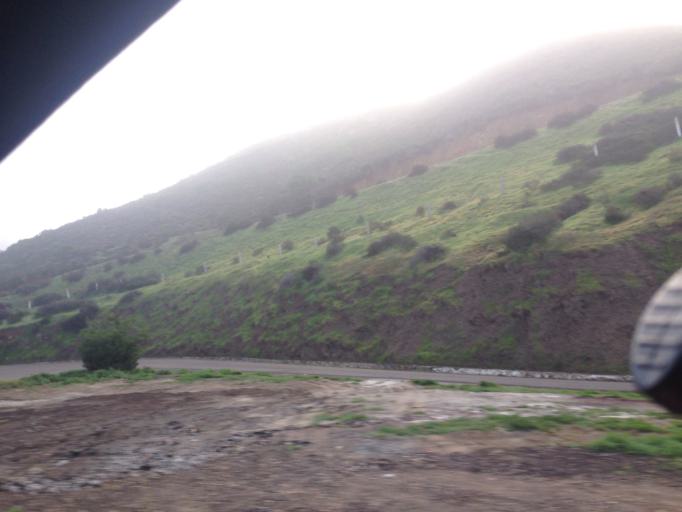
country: MX
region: Baja California
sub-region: Playas de Rosarito
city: Santa Anita
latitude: 32.1231
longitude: -116.8838
